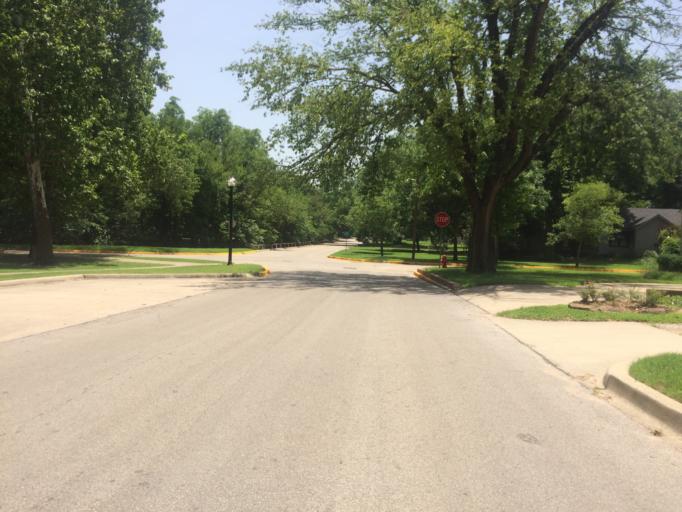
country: US
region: Oklahoma
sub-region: Cleveland County
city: Norman
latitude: 35.2134
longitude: -97.4547
